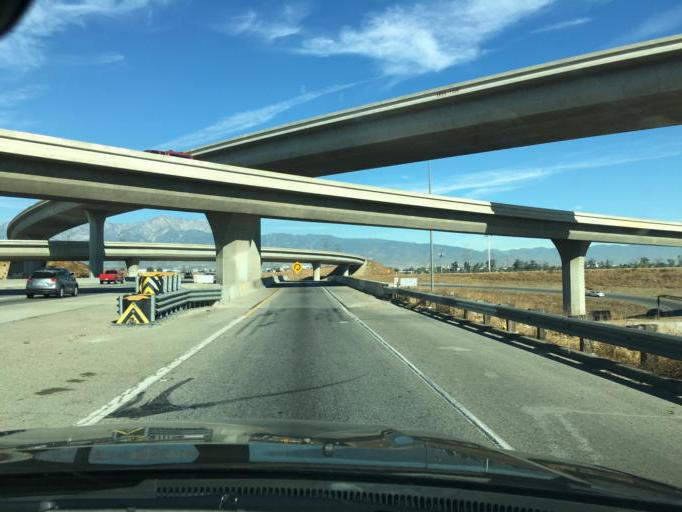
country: US
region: California
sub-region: Riverside County
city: Mira Loma
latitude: 34.0207
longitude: -117.5500
